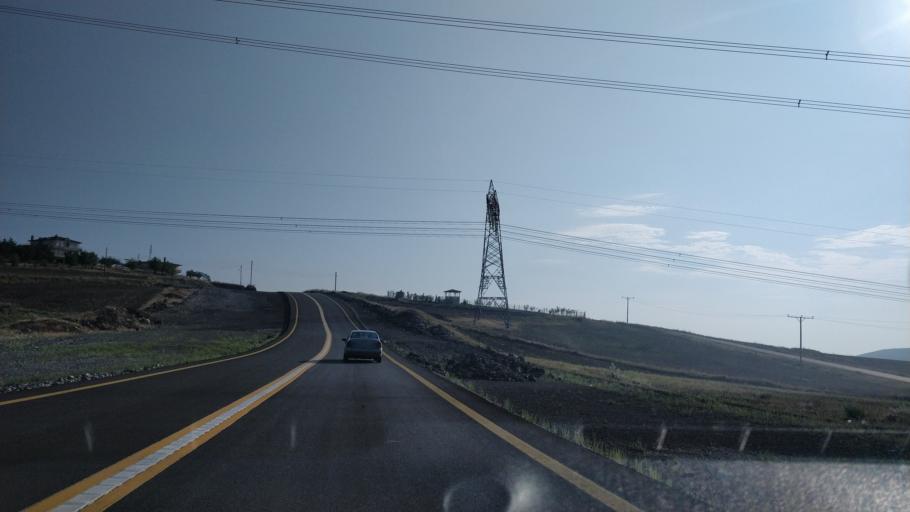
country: TR
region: Ankara
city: Etimesgut
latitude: 39.8661
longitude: 32.5875
